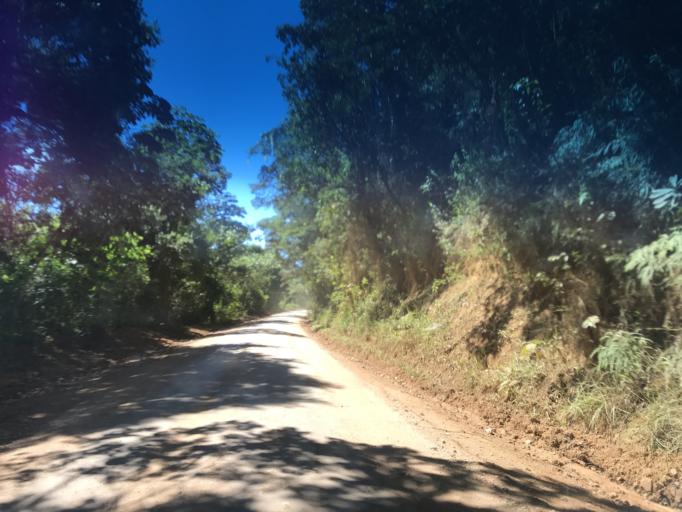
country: BR
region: Bahia
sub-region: Mutuipe
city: Mutuipe
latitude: -13.3740
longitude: -39.3771
